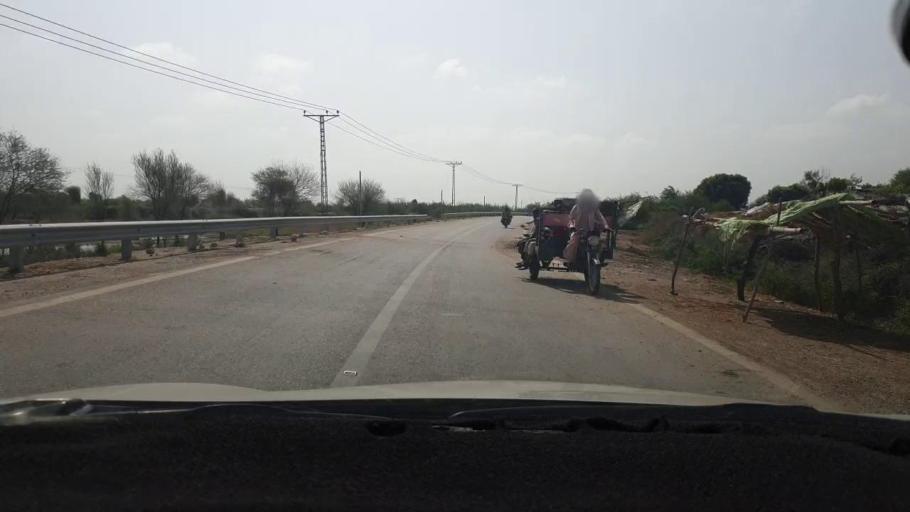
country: PK
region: Sindh
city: Mirpur Khas
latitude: 25.7578
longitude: 69.0836
